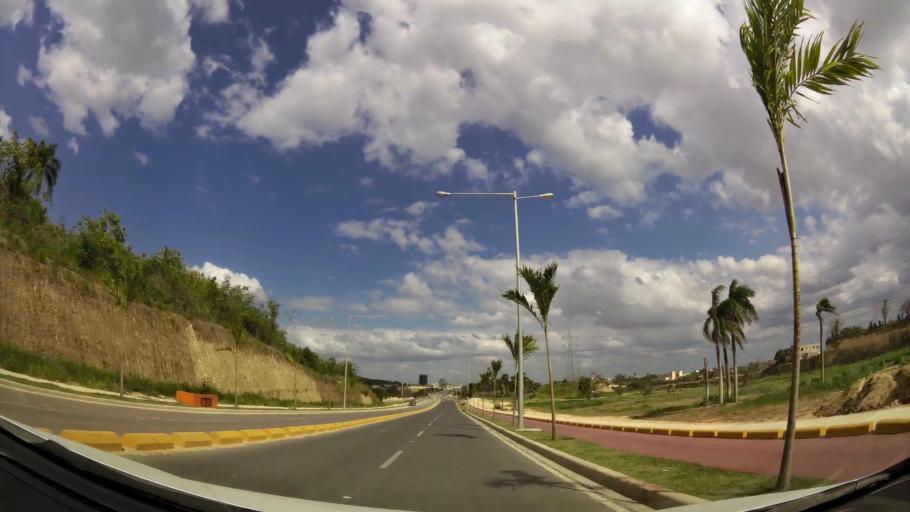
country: DO
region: Nacional
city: Ensanche Luperon
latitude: 18.5344
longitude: -69.8930
